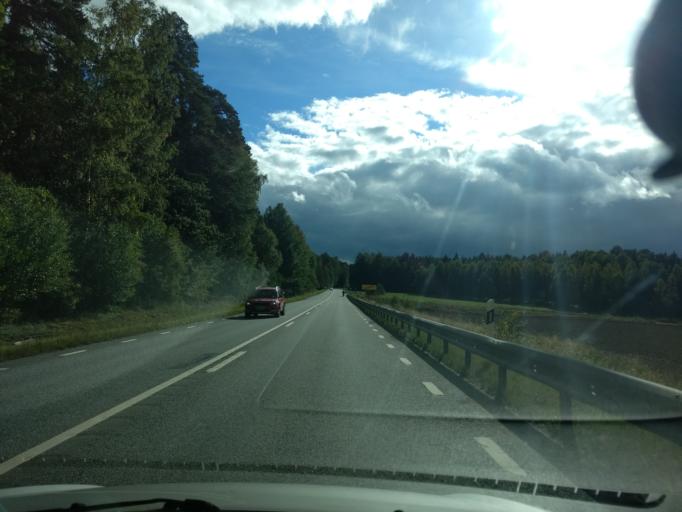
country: SE
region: Uppsala
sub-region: Uppsala Kommun
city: Saevja
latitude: 59.7816
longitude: 17.6640
